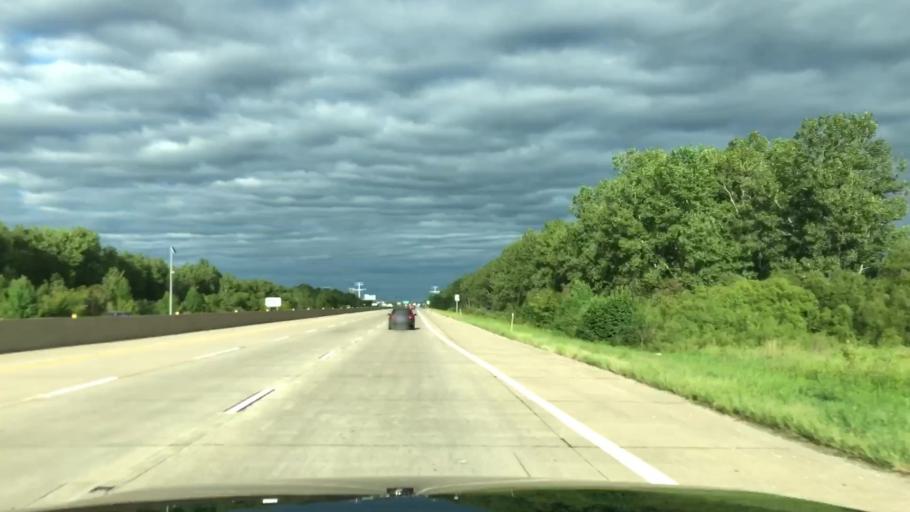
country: US
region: Missouri
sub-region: Saint Charles County
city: Saint Peters
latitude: 38.8187
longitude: -90.5545
